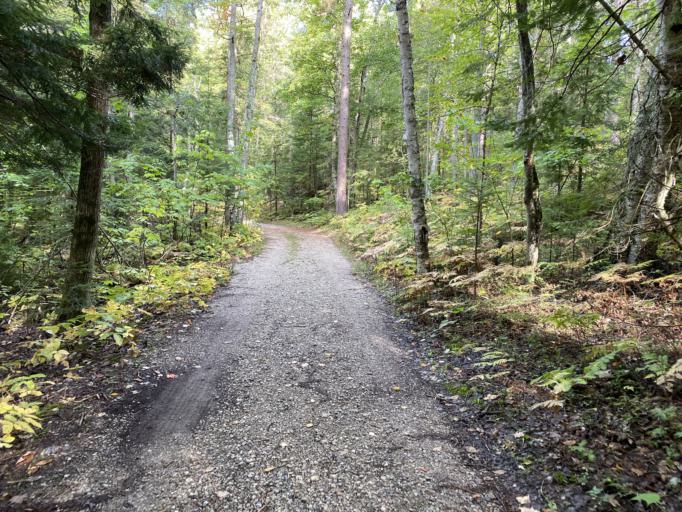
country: US
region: Michigan
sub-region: Mackinac County
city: Saint Ignace
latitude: 45.7472
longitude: -84.8787
